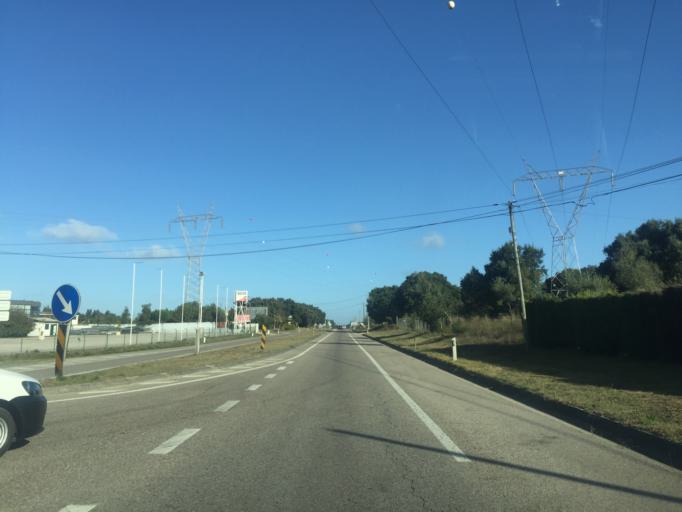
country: PT
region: Leiria
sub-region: Alcobaca
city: Benedita
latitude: 39.4061
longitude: -8.9616
